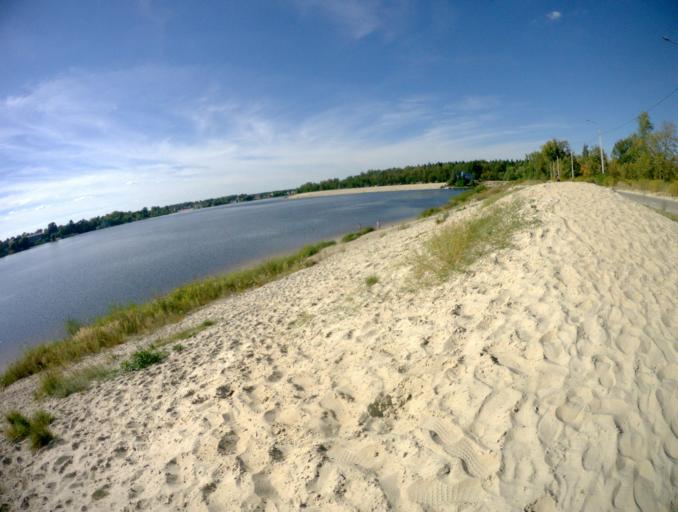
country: RU
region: Vladimir
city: Gus'-Khrustal'nyy
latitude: 55.6219
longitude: 40.6726
